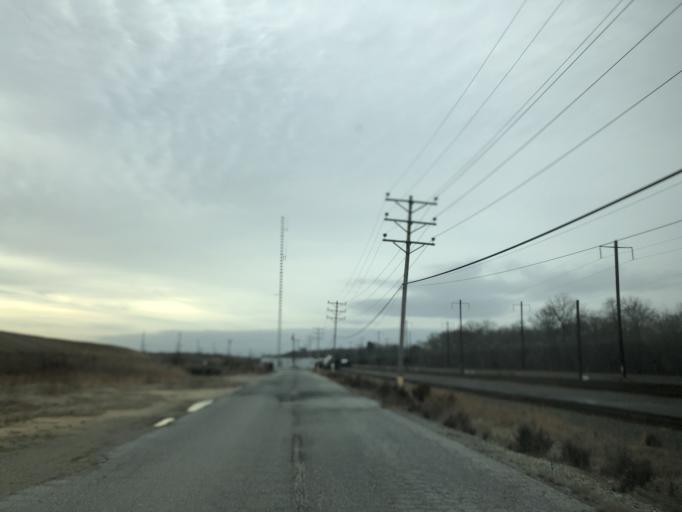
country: US
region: Delaware
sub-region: New Castle County
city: Newark
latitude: 39.6683
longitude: -75.7568
